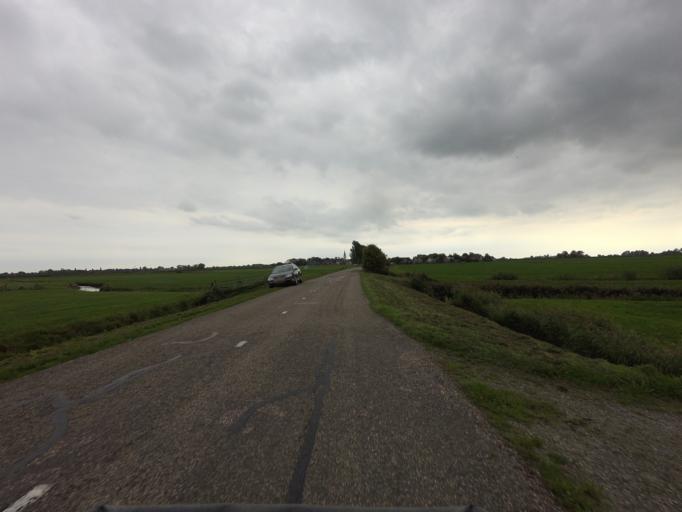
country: NL
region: Friesland
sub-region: Sudwest Fryslan
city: IJlst
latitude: 53.0223
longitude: 5.5981
